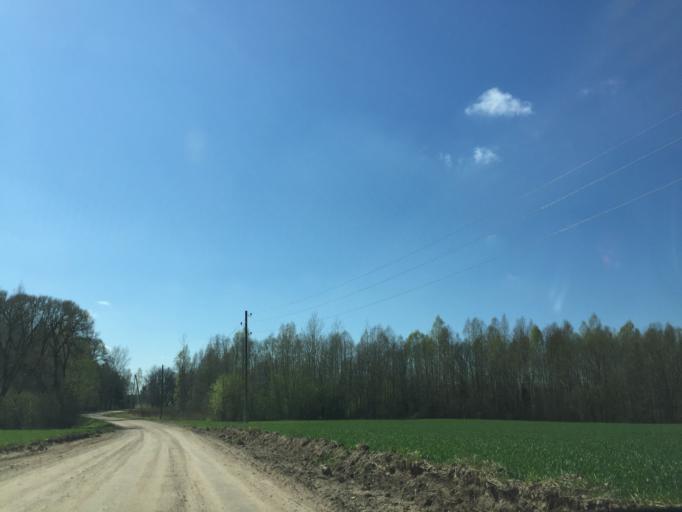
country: LV
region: Smiltene
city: Smiltene
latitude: 57.5629
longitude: 25.9018
